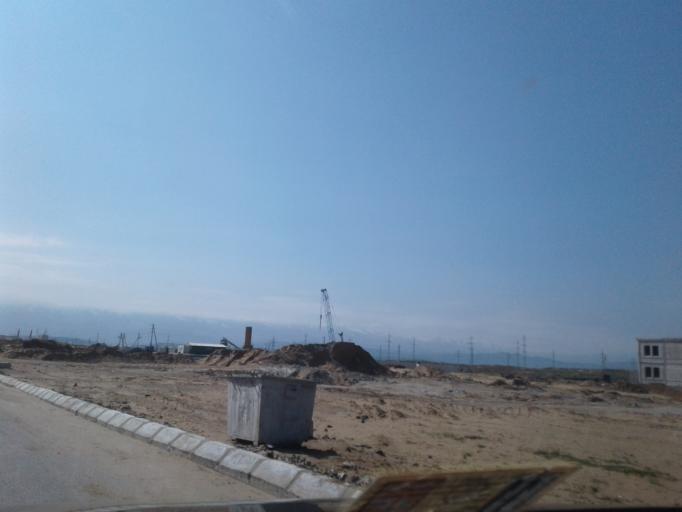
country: TM
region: Ahal
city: Ashgabat
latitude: 38.0113
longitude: 58.3932
